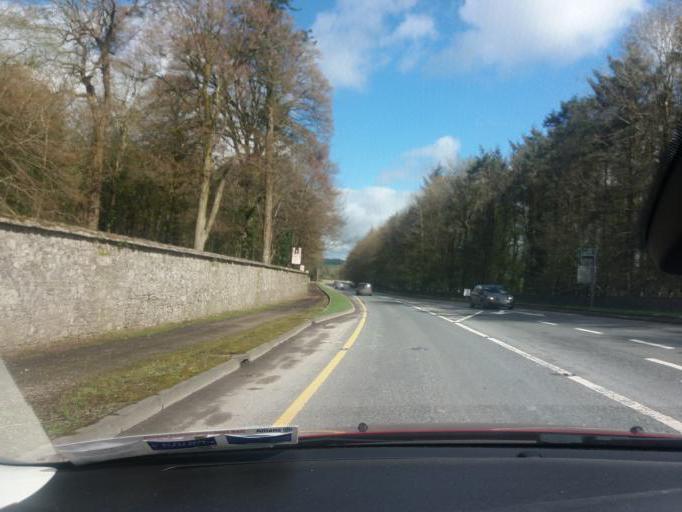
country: IE
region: Munster
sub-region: County Cork
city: Carrigtwohill
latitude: 51.8991
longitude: -8.2803
